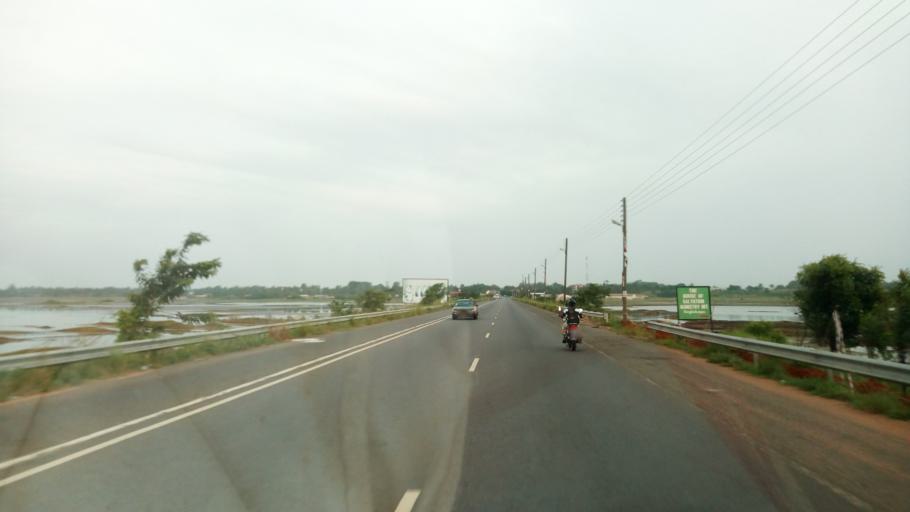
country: TG
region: Maritime
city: Lome
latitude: 6.1102
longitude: 1.1396
